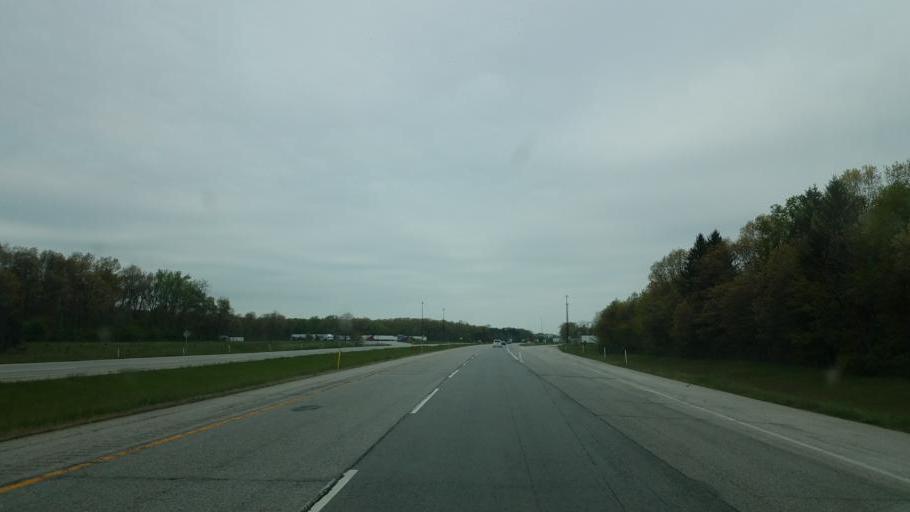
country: US
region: Michigan
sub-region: Saint Joseph County
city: White Pigeon
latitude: 41.7501
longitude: -85.6610
